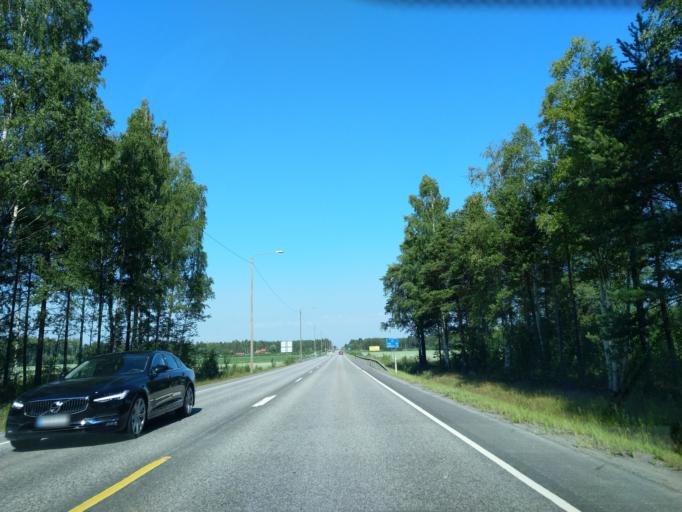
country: FI
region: Satakunta
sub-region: Pori
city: Harjavalta
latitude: 61.3098
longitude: 22.1195
